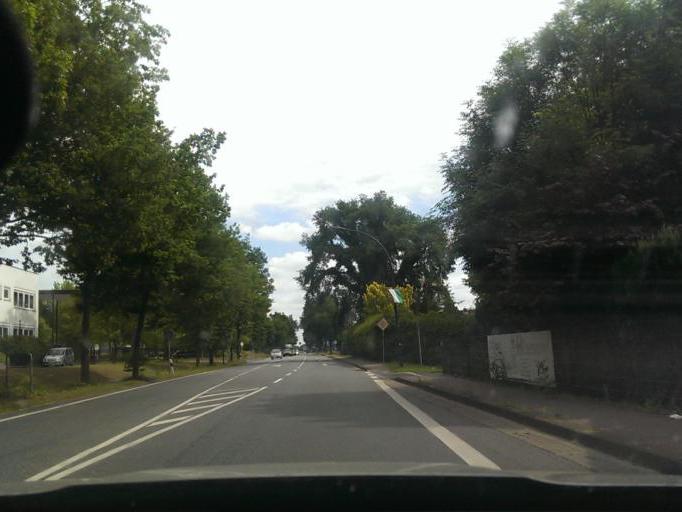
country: DE
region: Lower Saxony
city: Oyten
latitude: 53.0571
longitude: 9.0274
